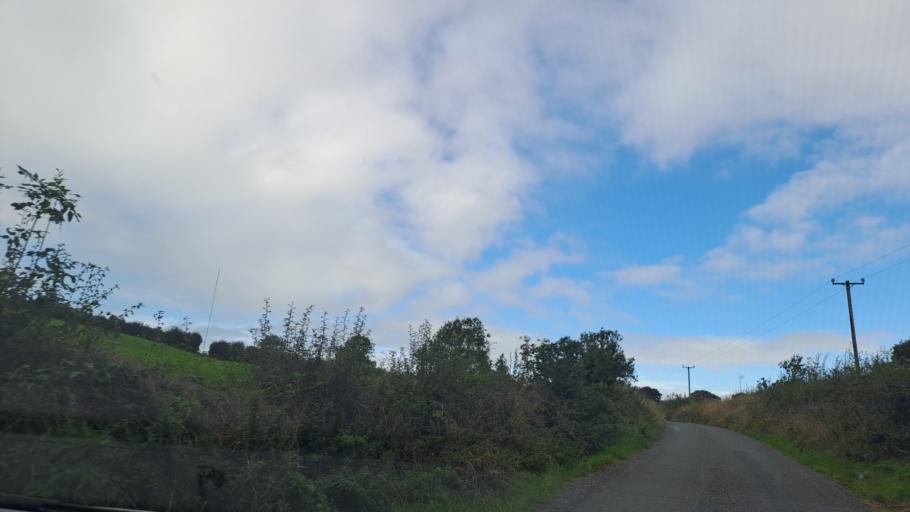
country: IE
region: Ulster
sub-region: An Cabhan
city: Kingscourt
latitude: 53.9944
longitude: -6.8061
